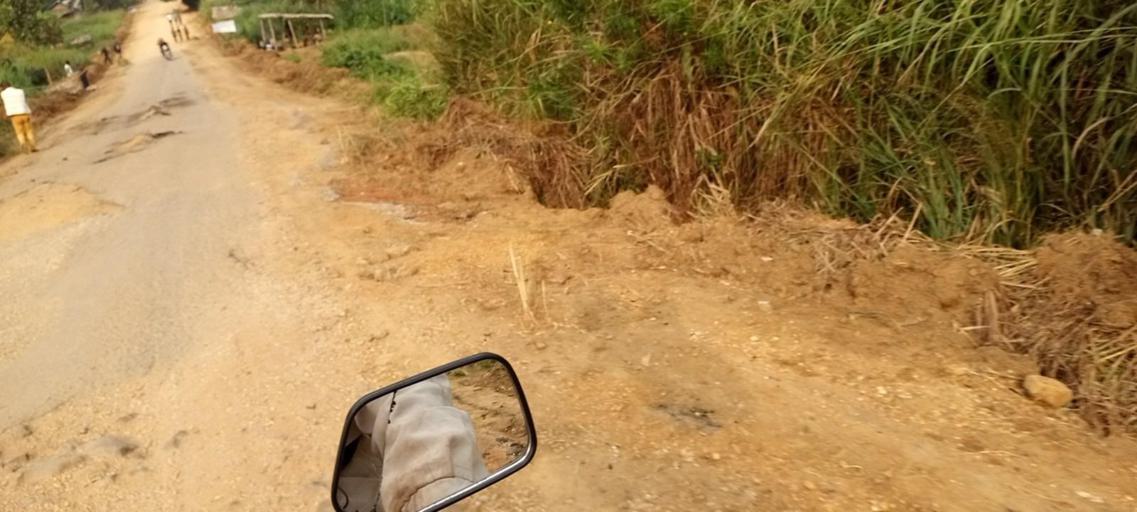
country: CD
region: Eastern Province
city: Kisangani
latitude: 0.1935
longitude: 25.5272
